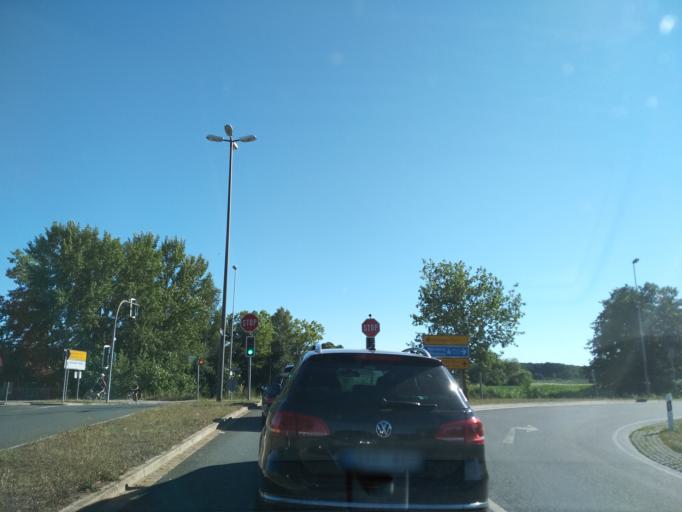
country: DE
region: Bavaria
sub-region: Regierungsbezirk Mittelfranken
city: Hessdorf
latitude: 49.6279
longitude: 10.9360
